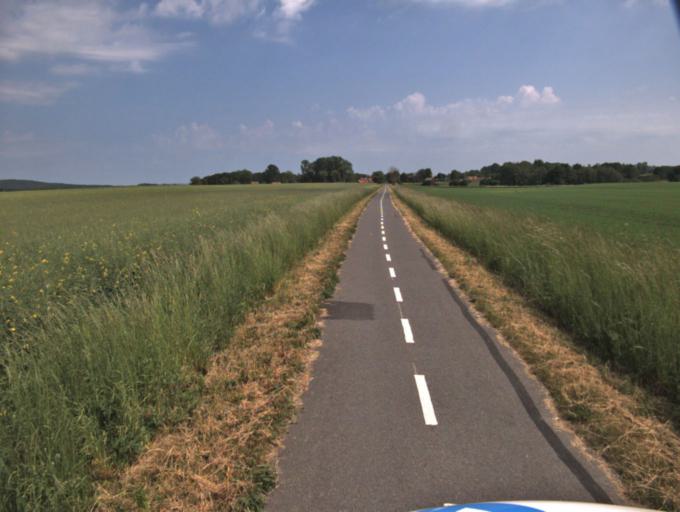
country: SE
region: Skane
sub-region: Kristianstads Kommun
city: Kristianstad
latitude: 56.0698
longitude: 14.1969
